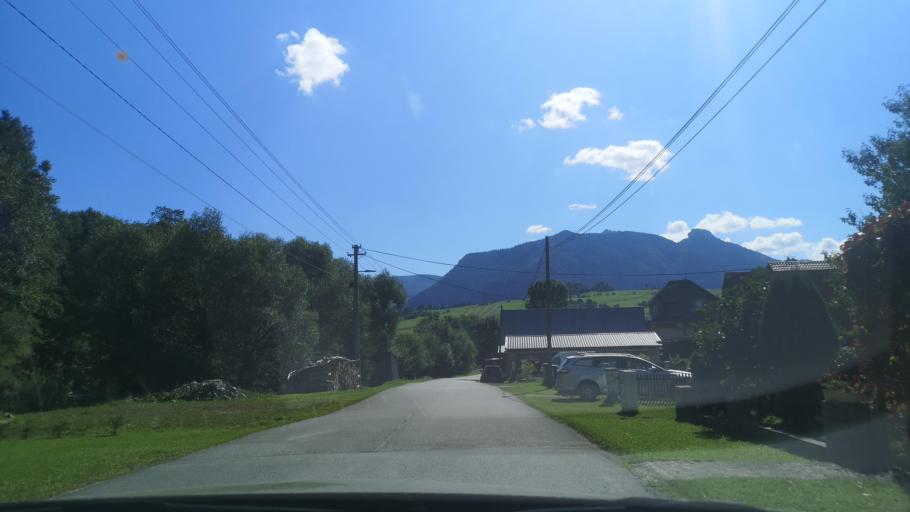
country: SK
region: Zilinsky
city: Oravska Lesna
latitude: 49.2833
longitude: 19.1347
